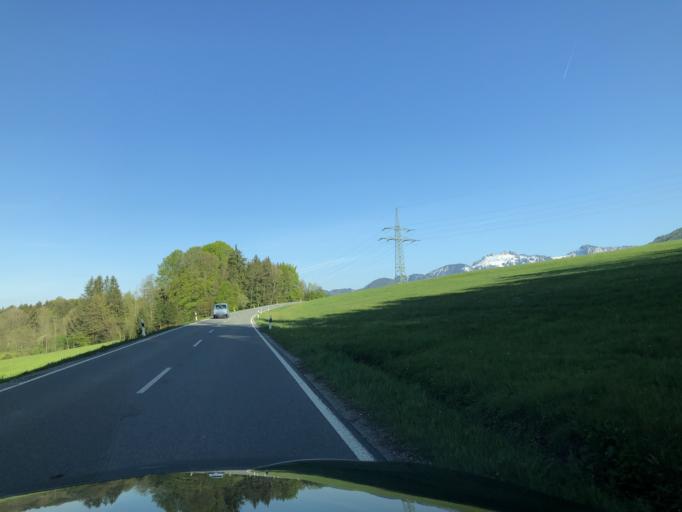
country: DE
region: Bavaria
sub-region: Upper Bavaria
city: Frasdorf
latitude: 47.8092
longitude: 12.2677
